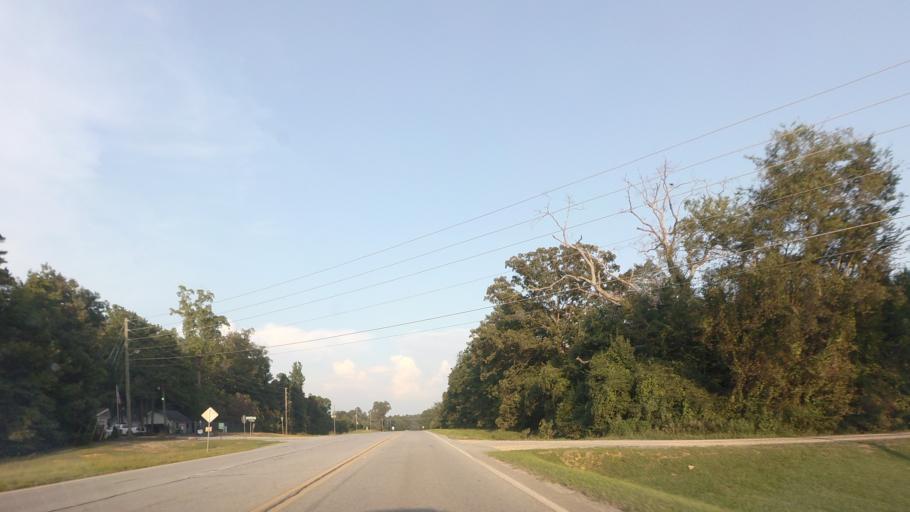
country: US
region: Georgia
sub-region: Bibb County
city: West Point
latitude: 32.8522
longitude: -83.7708
